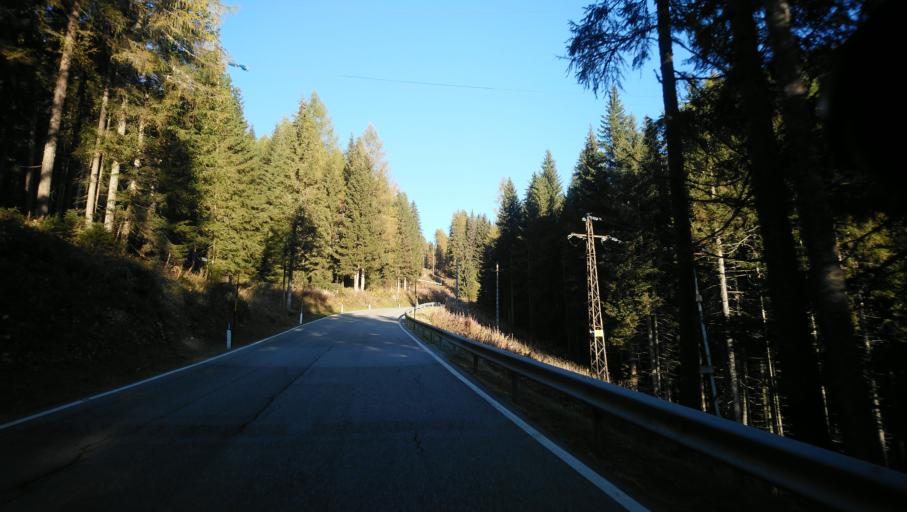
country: IT
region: Veneto
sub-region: Provincia di Belluno
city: Falcade Alto
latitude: 46.3663
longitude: 11.8312
